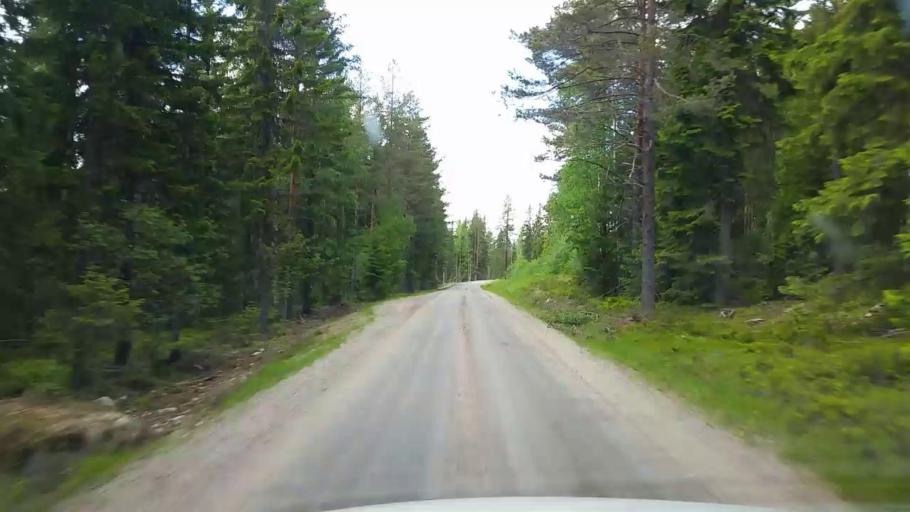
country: SE
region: Gaevleborg
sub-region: Ovanakers Kommun
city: Edsbyn
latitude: 61.5657
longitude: 15.9580
